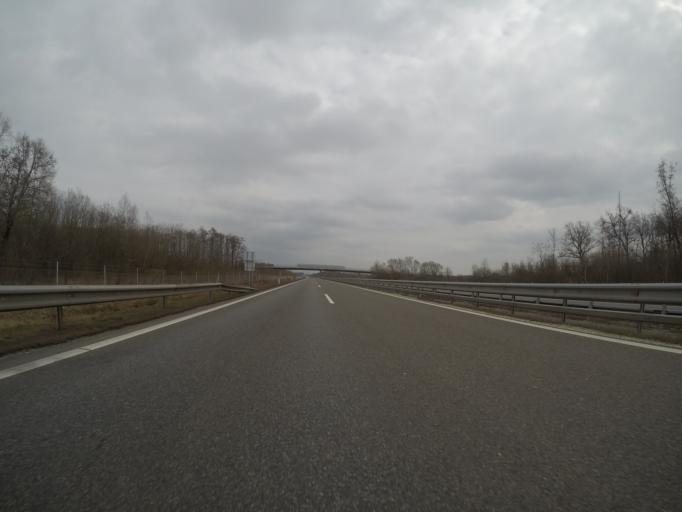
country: SI
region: Turnisce
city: Turnisce
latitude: 46.6041
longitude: 16.3329
